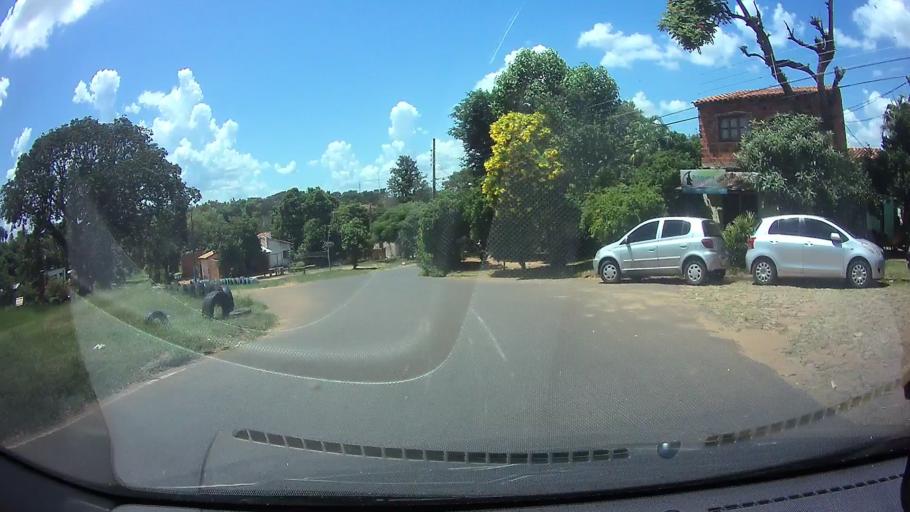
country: PY
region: Central
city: Limpio
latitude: -25.1517
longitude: -57.4518
